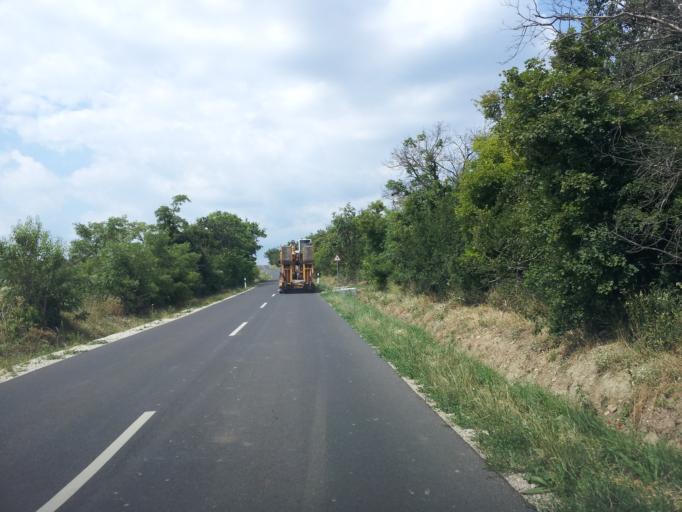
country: HU
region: Veszprem
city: Zanka
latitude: 46.8871
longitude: 17.7438
